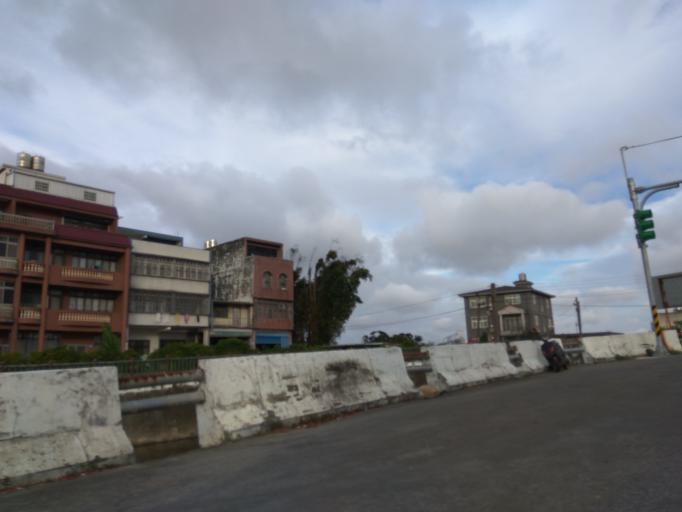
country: TW
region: Taiwan
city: Daxi
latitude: 24.9212
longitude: 121.1959
